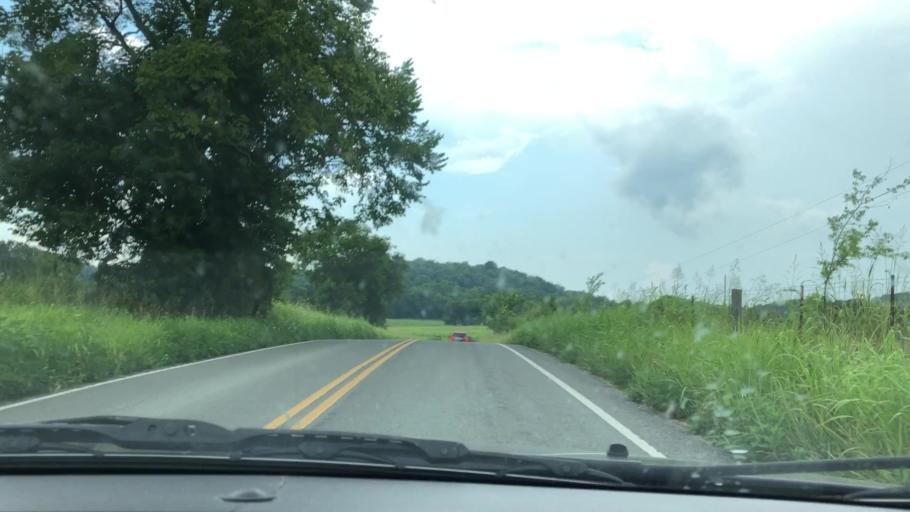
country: US
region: Tennessee
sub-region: Maury County
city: Spring Hill
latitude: 35.7821
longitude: -87.0039
